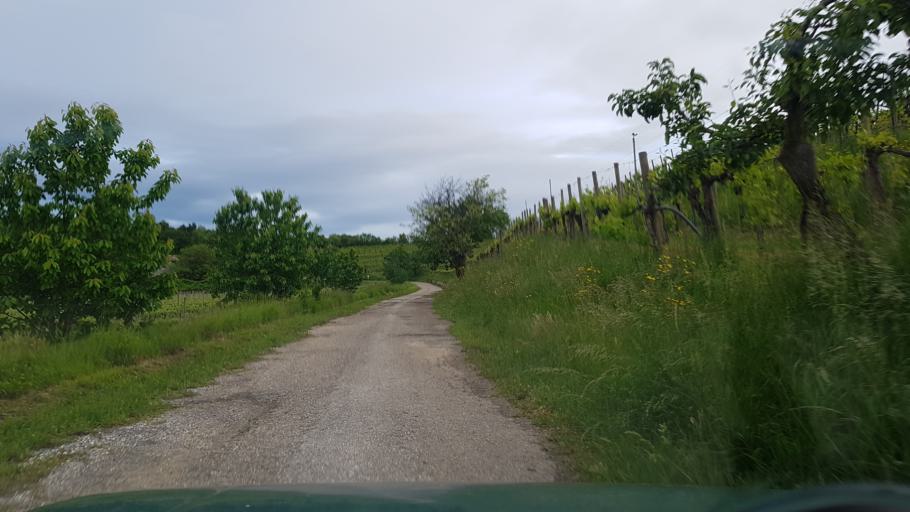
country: IT
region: Friuli Venezia Giulia
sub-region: Provincia di Gorizia
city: Farra d'Isonzo
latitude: 45.9094
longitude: 13.5291
